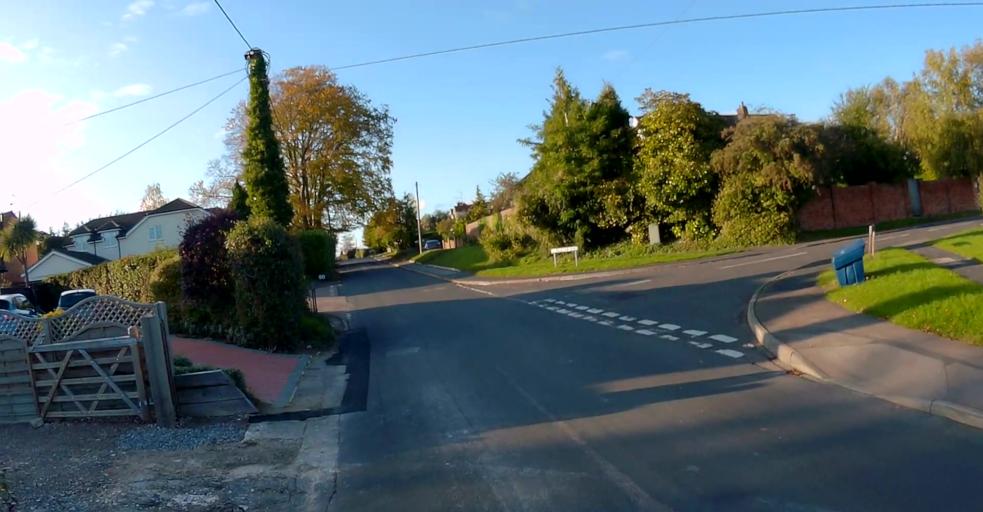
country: GB
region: England
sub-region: Hampshire
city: Old Basing
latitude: 51.2650
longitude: -1.0355
